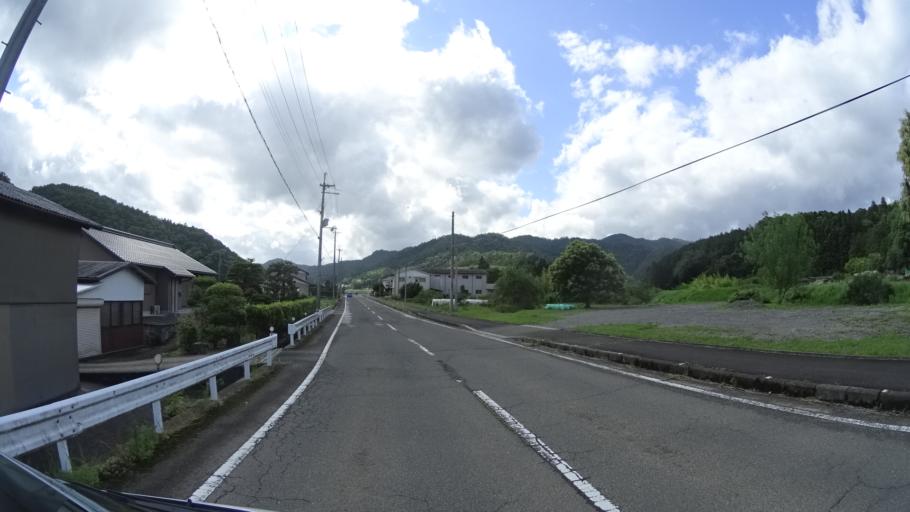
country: JP
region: Kyoto
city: Ayabe
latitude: 35.3735
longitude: 135.2390
